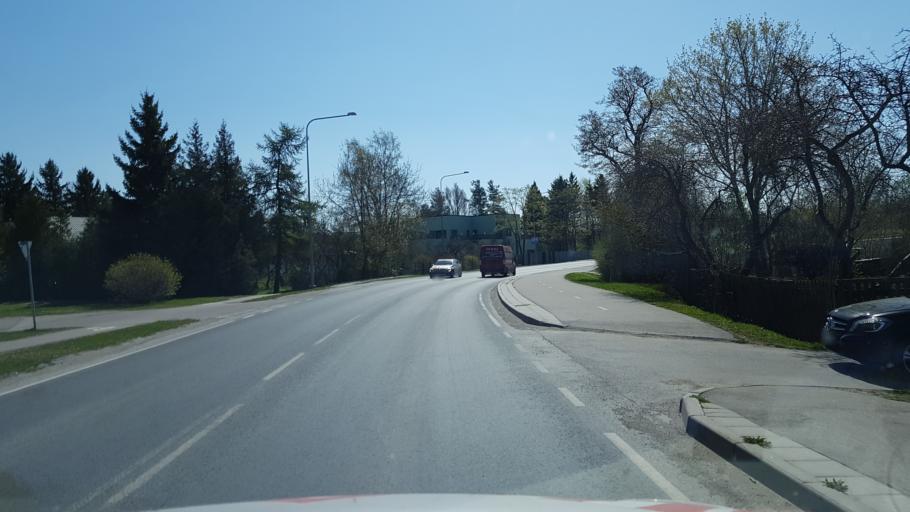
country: EE
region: Harju
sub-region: Viimsi vald
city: Haabneeme
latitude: 59.5098
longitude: 24.8220
